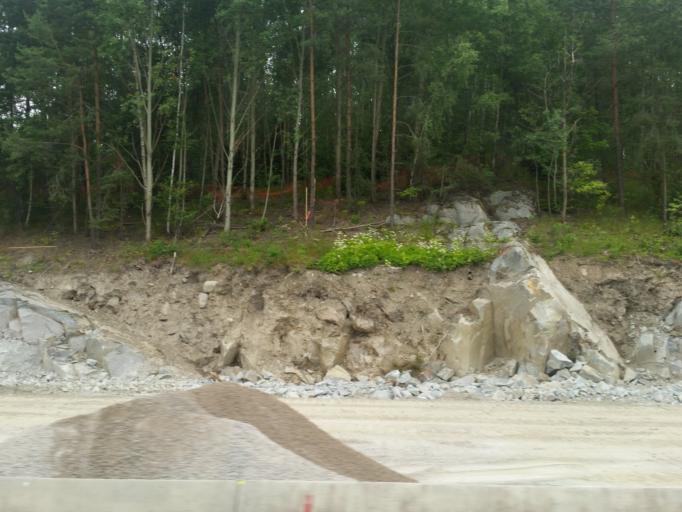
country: SE
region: Stockholm
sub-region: Stockholms Kommun
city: Kista
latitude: 59.4170
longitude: 17.9061
